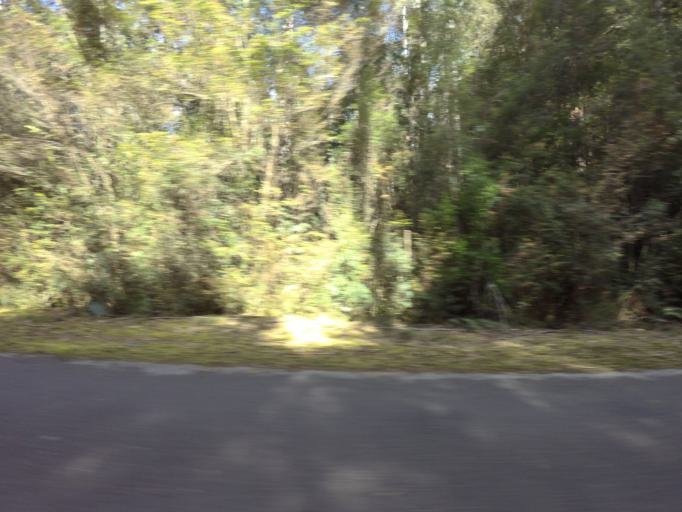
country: AU
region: Tasmania
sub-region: Huon Valley
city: Geeveston
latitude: -42.8269
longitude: 146.3168
